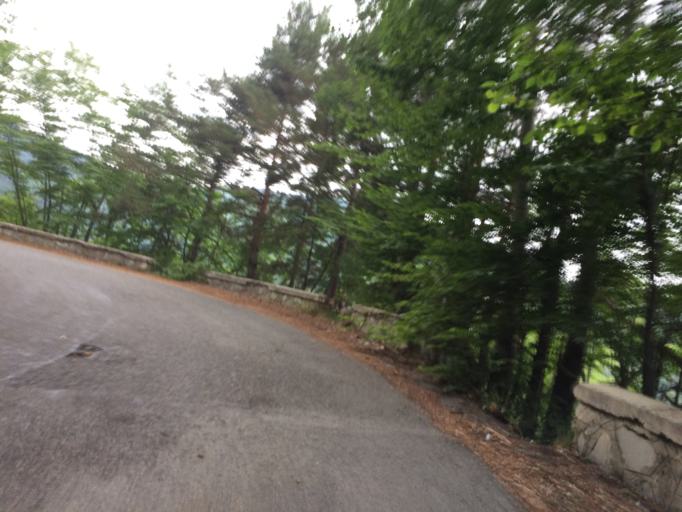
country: IT
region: Liguria
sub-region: Provincia di Imperia
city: Triora
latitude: 43.9730
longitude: 7.7442
